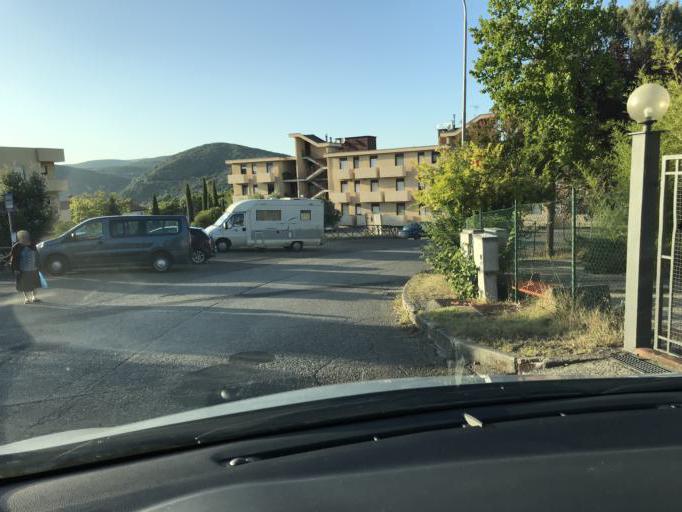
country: IT
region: Umbria
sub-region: Provincia di Terni
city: Amelia
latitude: 42.5461
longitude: 12.4147
